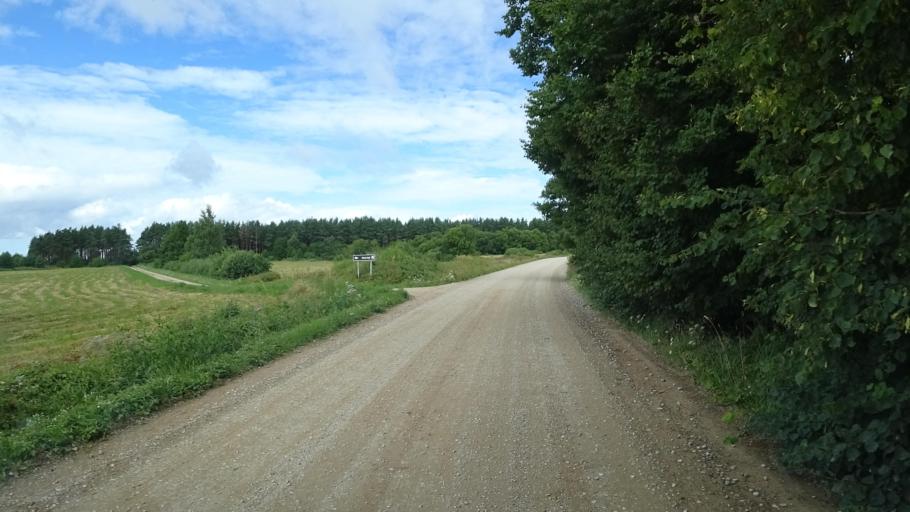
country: LV
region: Liepaja
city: Vec-Liepaja
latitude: 56.6320
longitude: 21.0482
